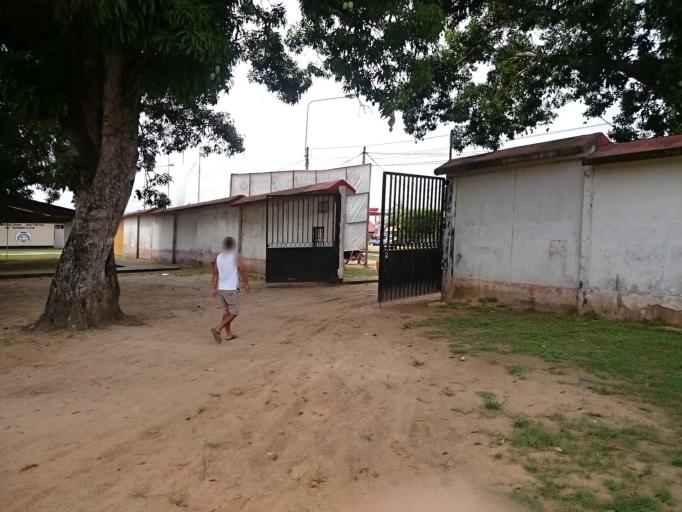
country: PE
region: Ucayali
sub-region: Provincia de Coronel Portillo
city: Puerto Callao
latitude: -8.3614
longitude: -74.5691
